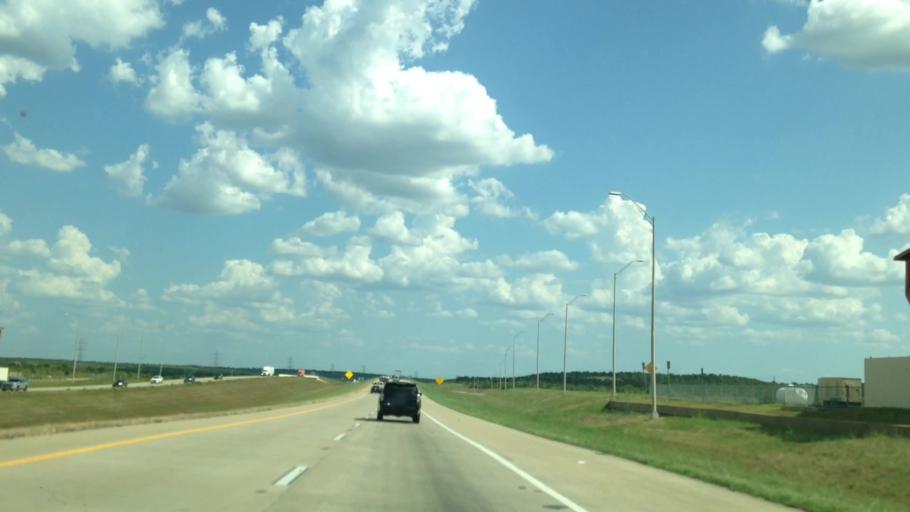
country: US
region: Texas
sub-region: Travis County
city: Manor
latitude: 30.3264
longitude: -97.5844
